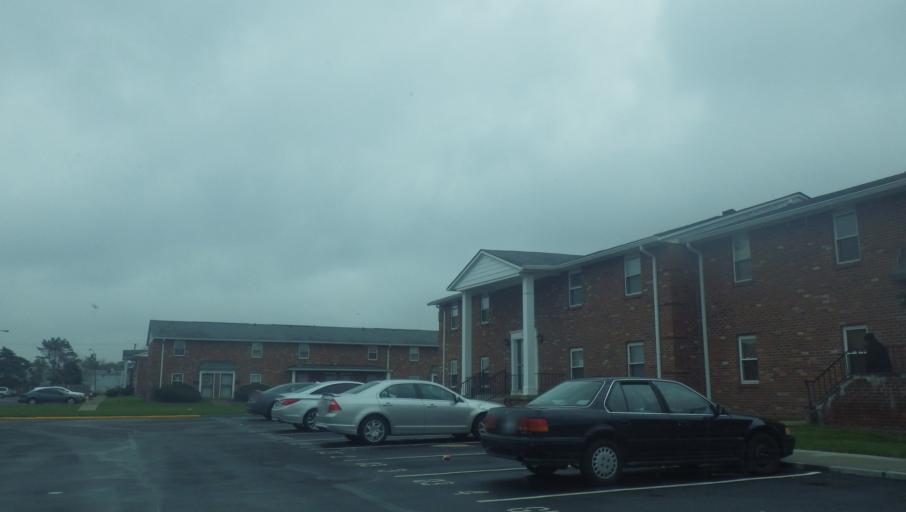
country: US
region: Indiana
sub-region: Marion County
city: Cumberland
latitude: 39.7978
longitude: -85.9945
